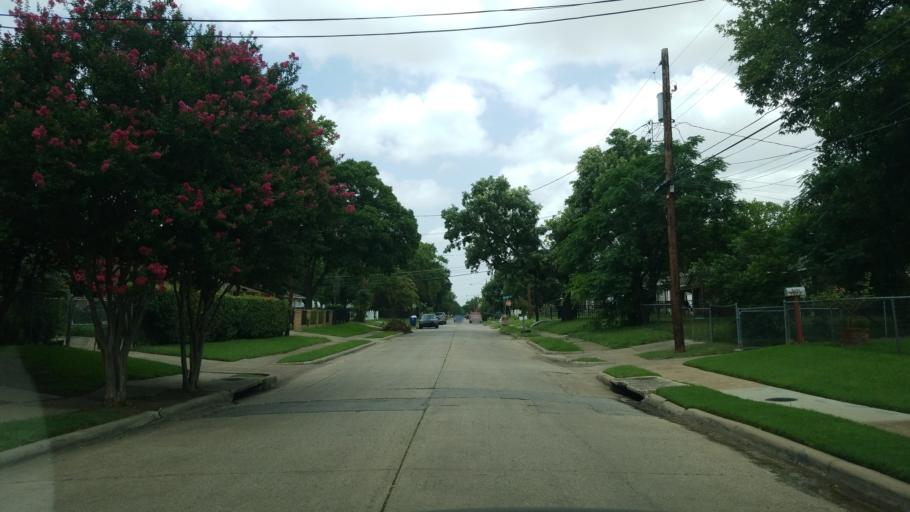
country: US
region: Texas
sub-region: Dallas County
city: Cockrell Hill
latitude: 32.7842
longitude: -96.9046
